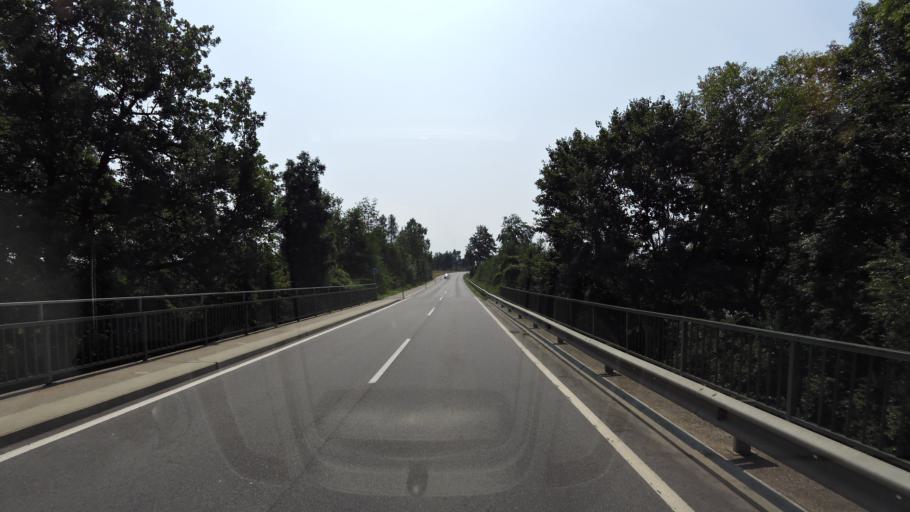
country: DE
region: Bavaria
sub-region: Lower Bavaria
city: Bad Fussing
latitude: 48.3105
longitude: 13.3278
